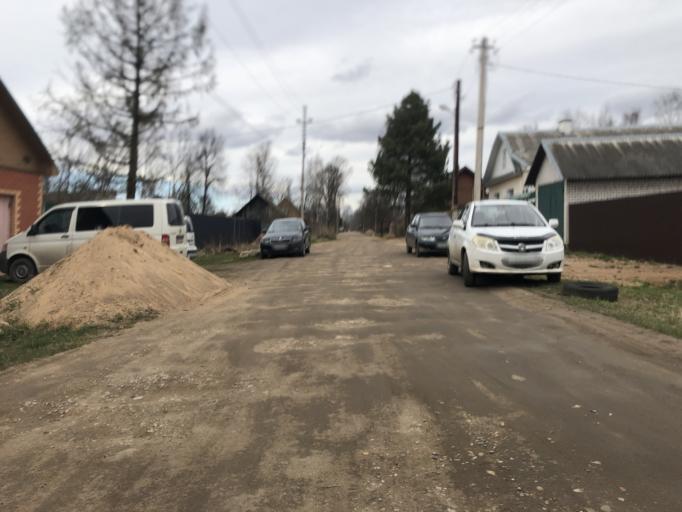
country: RU
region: Tverskaya
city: Rzhev
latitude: 56.2505
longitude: 34.3171
